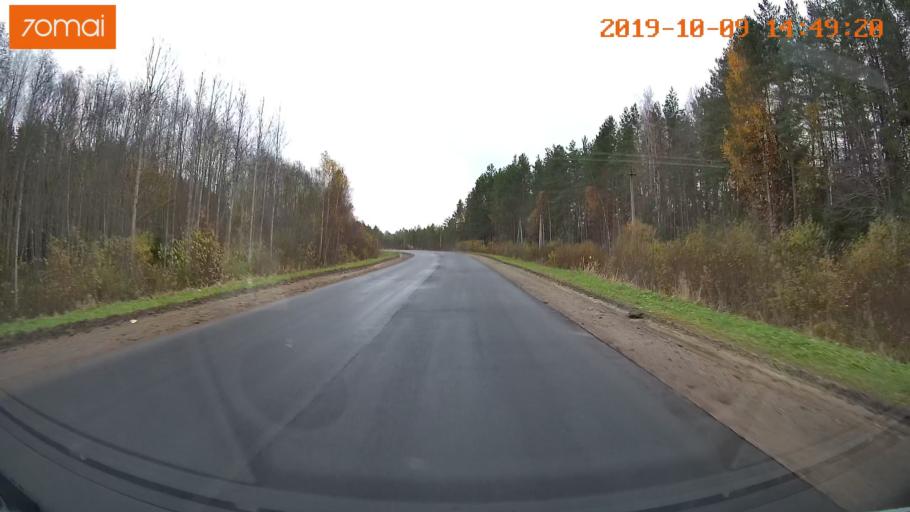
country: RU
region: Kostroma
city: Chistyye Bory
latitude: 58.3944
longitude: 41.5810
